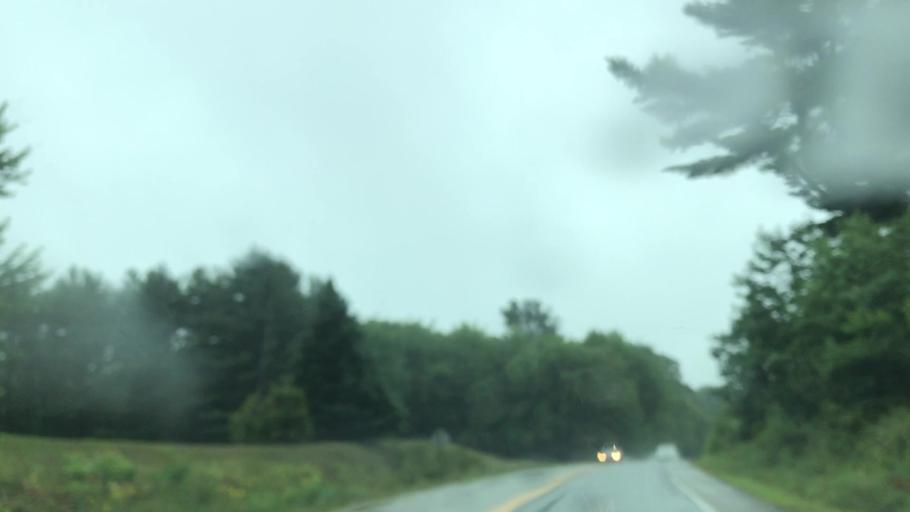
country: US
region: Maine
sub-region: York County
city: North Berwick
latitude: 43.2970
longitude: -70.7821
